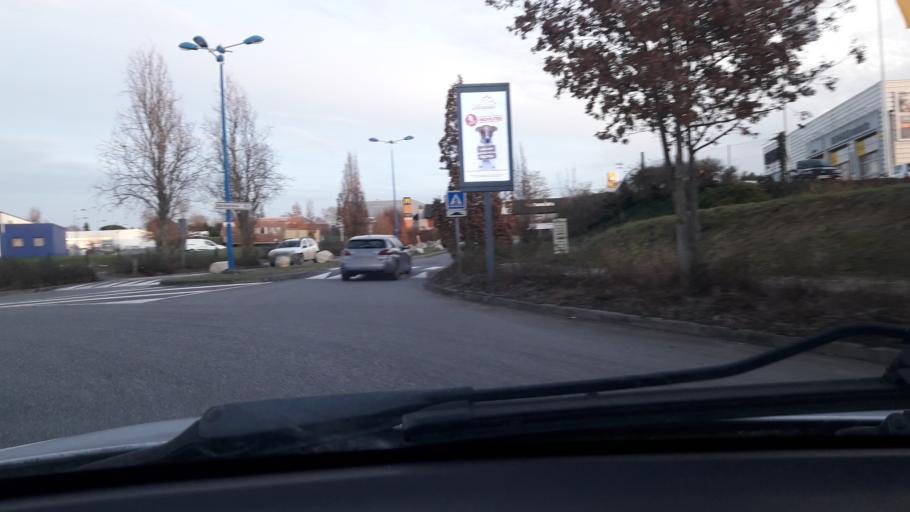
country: FR
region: Midi-Pyrenees
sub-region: Departement du Gers
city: Pujaudran
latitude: 43.6044
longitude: 1.0715
